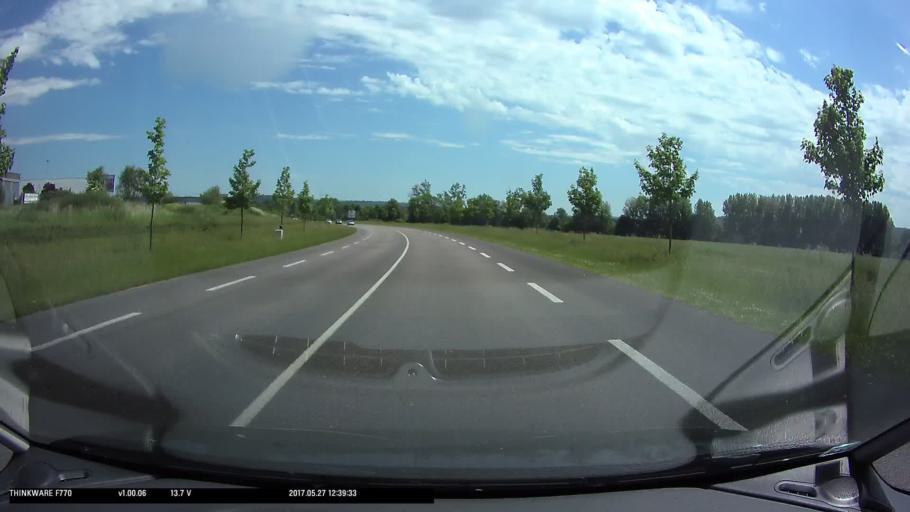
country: FR
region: Haute-Normandie
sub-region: Departement de l'Eure
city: Gisors
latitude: 49.2752
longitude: 1.7581
